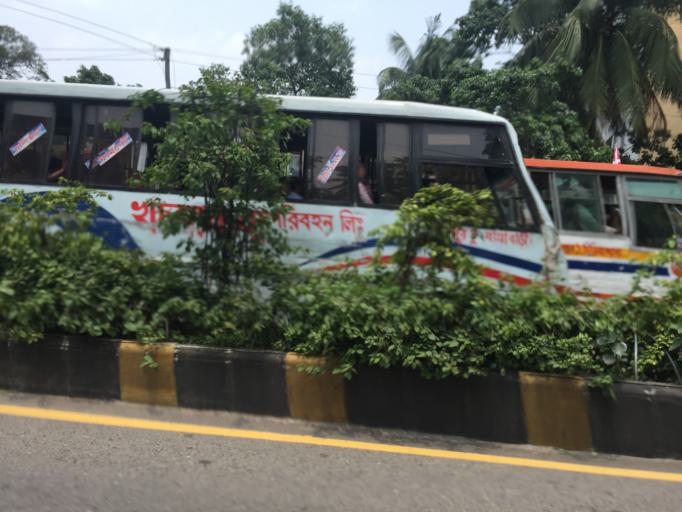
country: BD
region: Dhaka
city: Paltan
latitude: 23.7329
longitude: 90.4043
